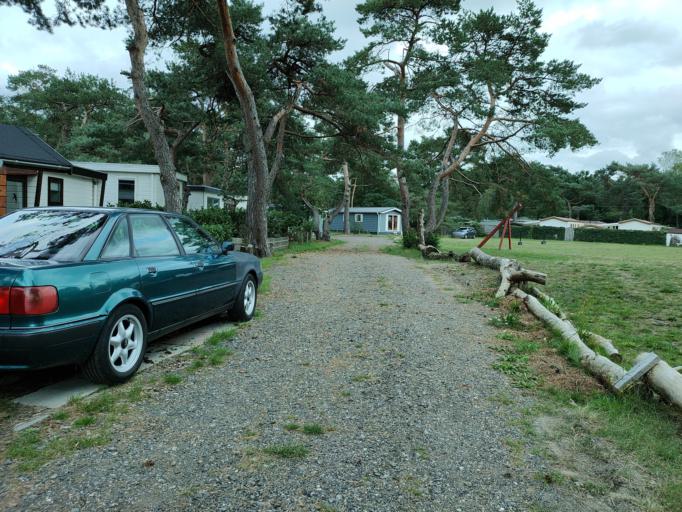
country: NL
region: Utrecht
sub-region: Gemeente Zeist
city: Zeist
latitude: 52.1310
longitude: 5.2255
